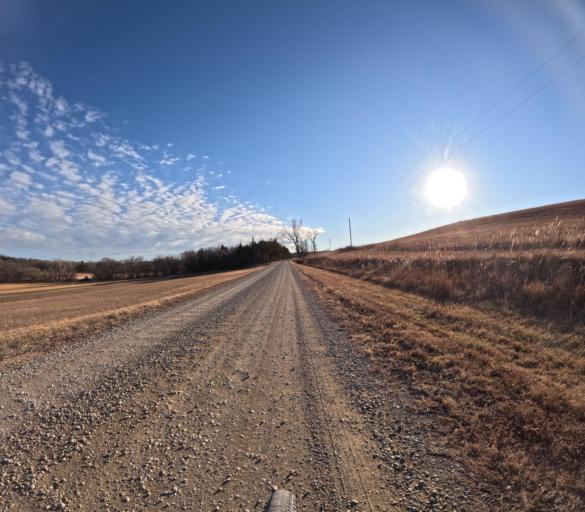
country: US
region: Kansas
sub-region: Riley County
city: Ogden
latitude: 39.2145
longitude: -96.6786
